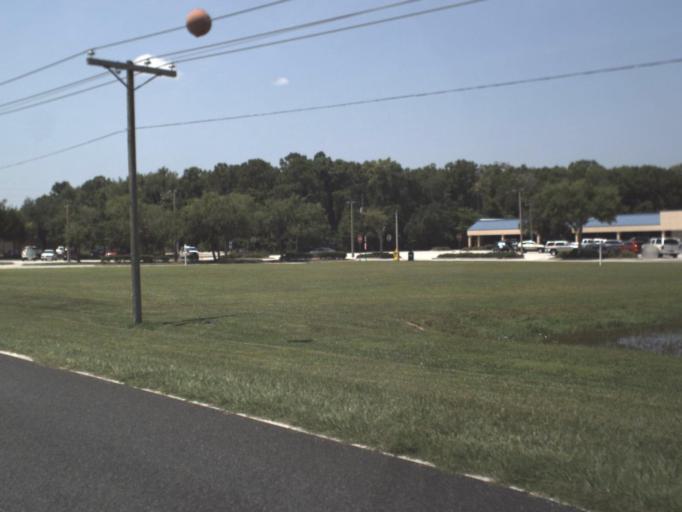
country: US
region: Florida
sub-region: Citrus County
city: Crystal River
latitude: 28.8672
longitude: -82.5798
